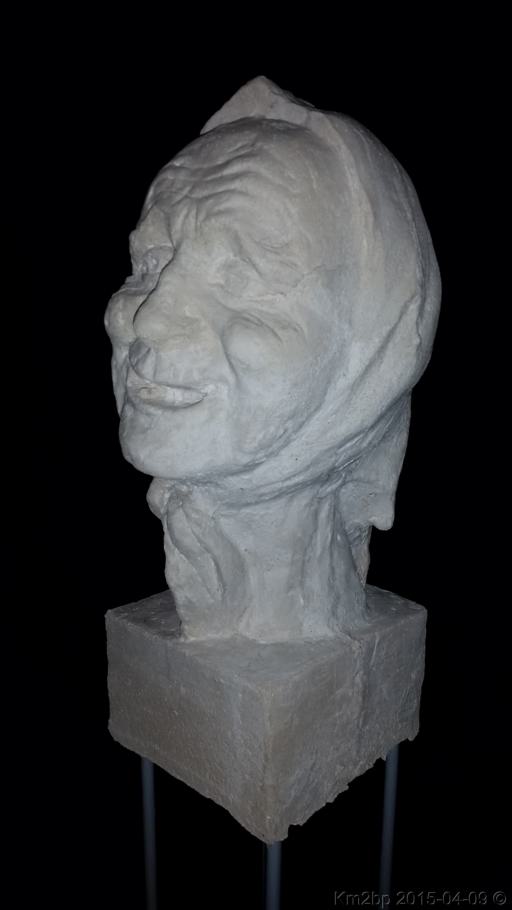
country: PL
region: Lubusz
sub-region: Zielona Gora
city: Zielona Gora
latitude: 51.9491
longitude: 15.5011
